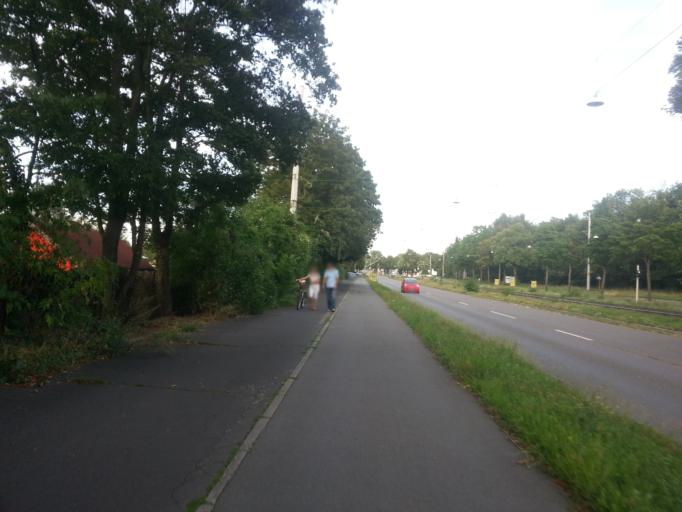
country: DE
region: Baden-Wuerttemberg
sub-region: Karlsruhe Region
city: Mannheim
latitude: 49.4897
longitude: 8.4973
